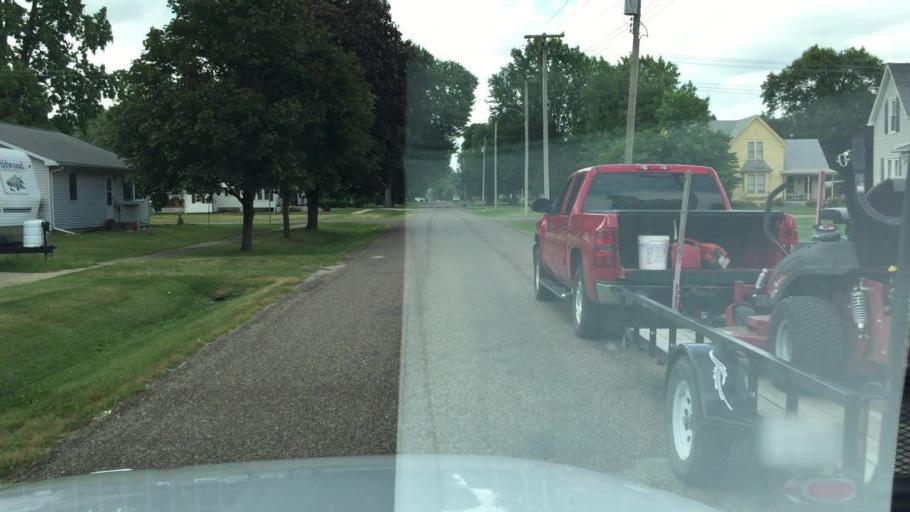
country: US
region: Illinois
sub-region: Hancock County
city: Carthage
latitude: 40.4175
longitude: -91.1380
